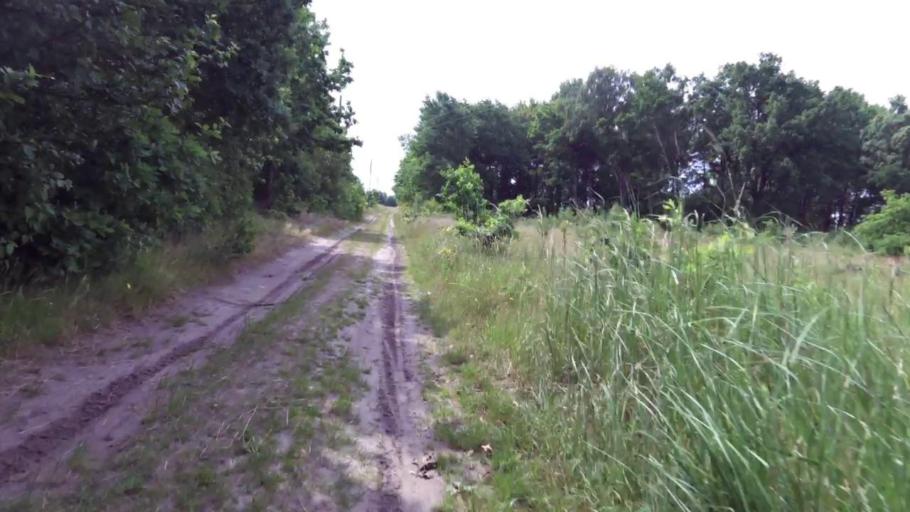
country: PL
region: West Pomeranian Voivodeship
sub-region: Powiat kamienski
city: Wolin
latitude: 53.7601
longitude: 14.6496
